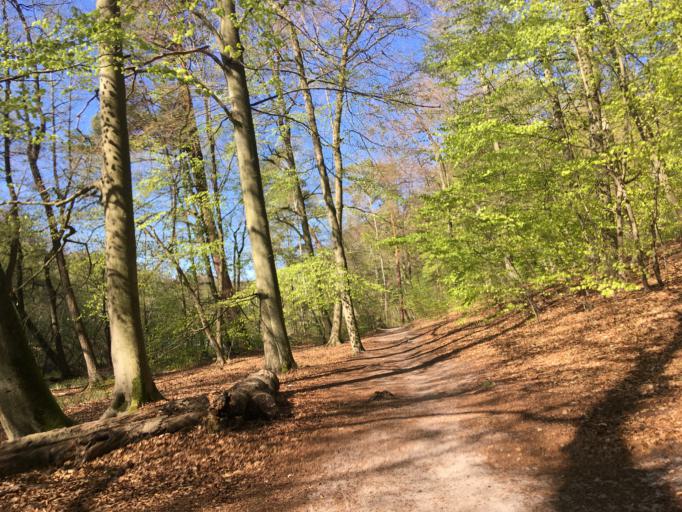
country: DE
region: Brandenburg
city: Wandlitz
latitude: 52.7509
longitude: 13.5040
